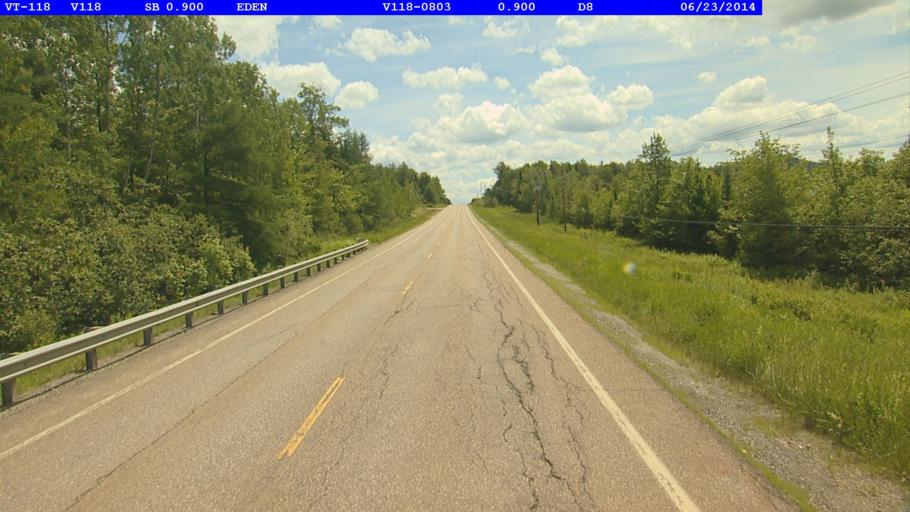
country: US
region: Vermont
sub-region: Lamoille County
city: Hyde Park
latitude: 44.7178
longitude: -72.5565
